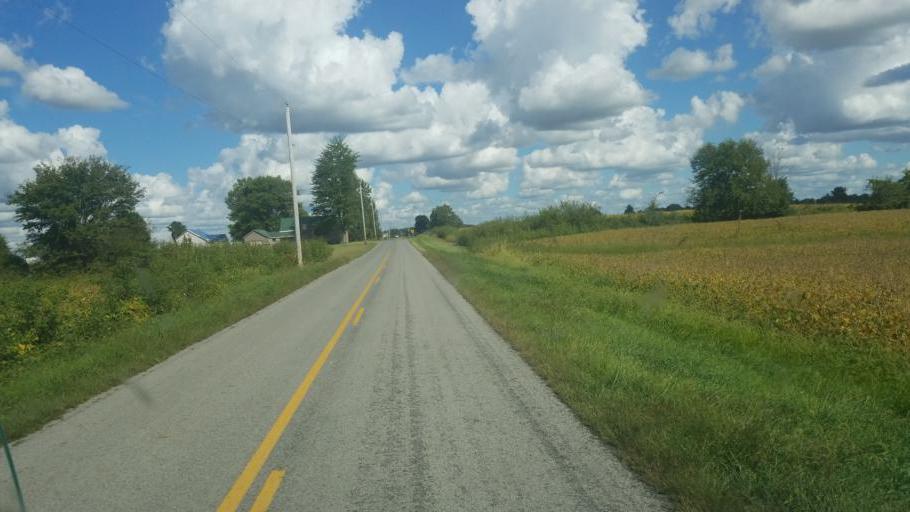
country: US
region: Ohio
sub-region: Hardin County
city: Kenton
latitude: 40.5069
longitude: -83.5669
